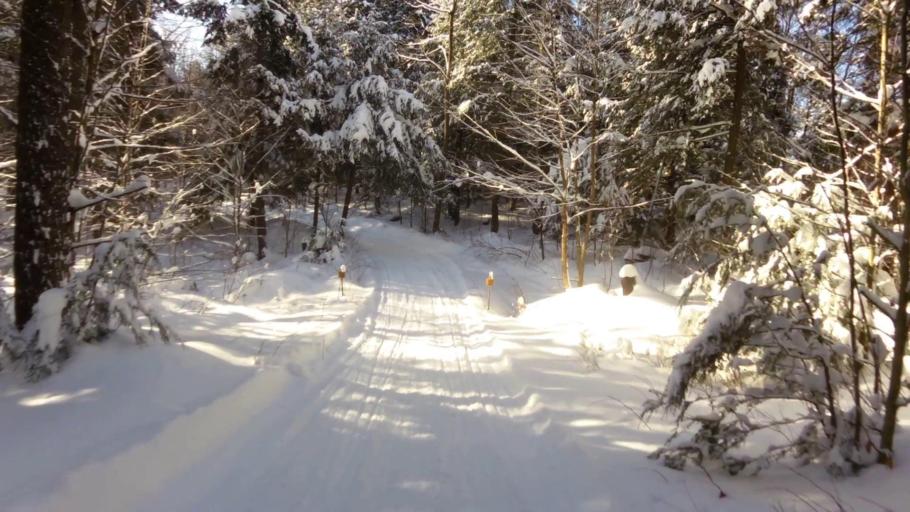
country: US
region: New York
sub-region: Chautauqua County
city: Falconer
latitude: 42.2629
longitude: -79.1193
